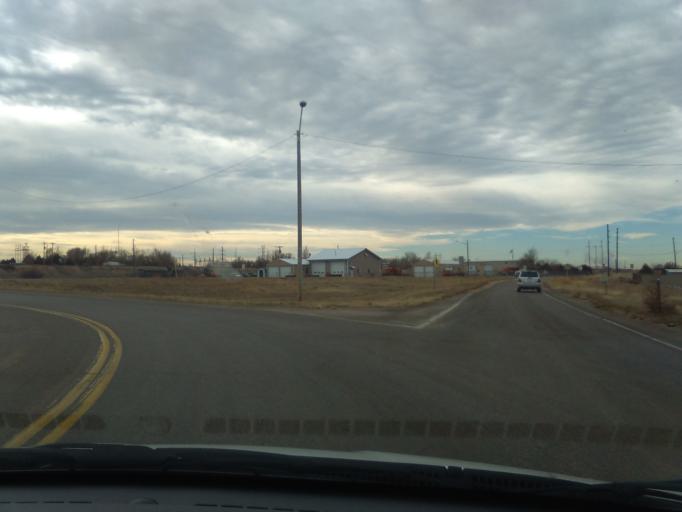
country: US
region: Colorado
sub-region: Morgan County
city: Brush
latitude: 40.2617
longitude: -103.5940
